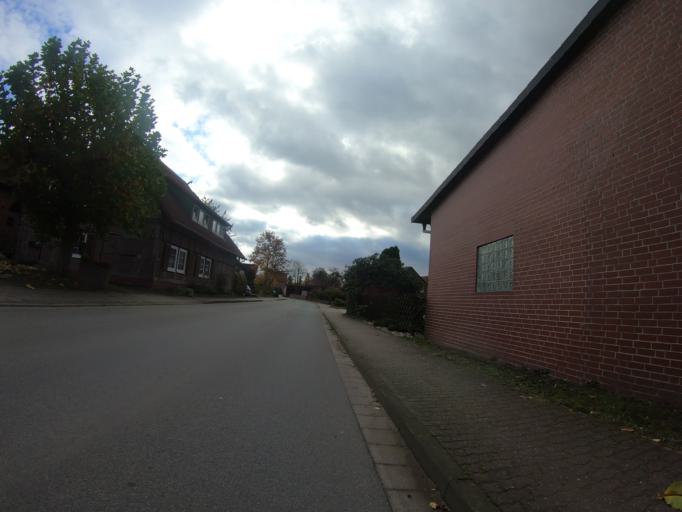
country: DE
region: Lower Saxony
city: Ribbesbuttel
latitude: 52.4250
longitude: 10.4837
